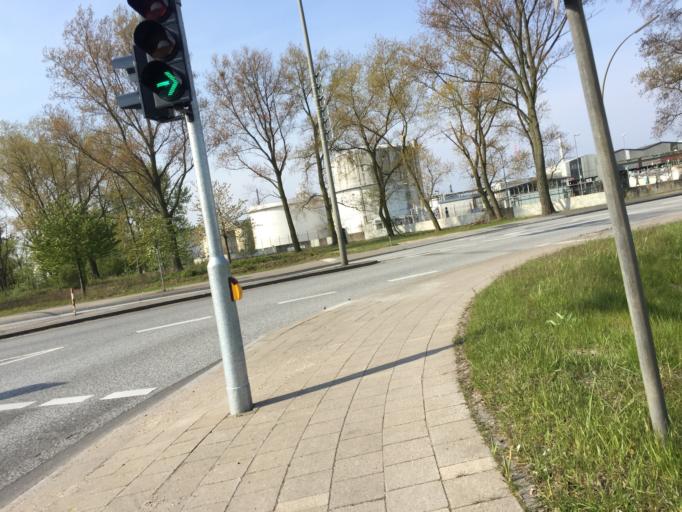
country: DE
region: Hamburg
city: Harburg
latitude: 53.4913
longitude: 9.9759
